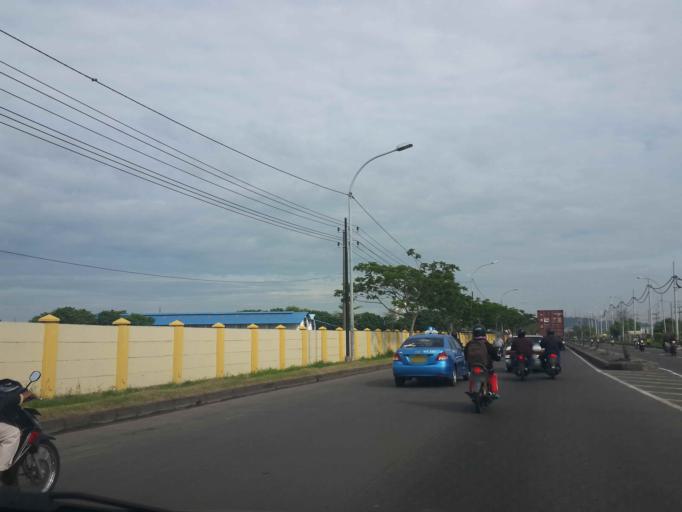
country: ID
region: East Java
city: Kebomas
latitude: -7.2088
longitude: 112.6517
